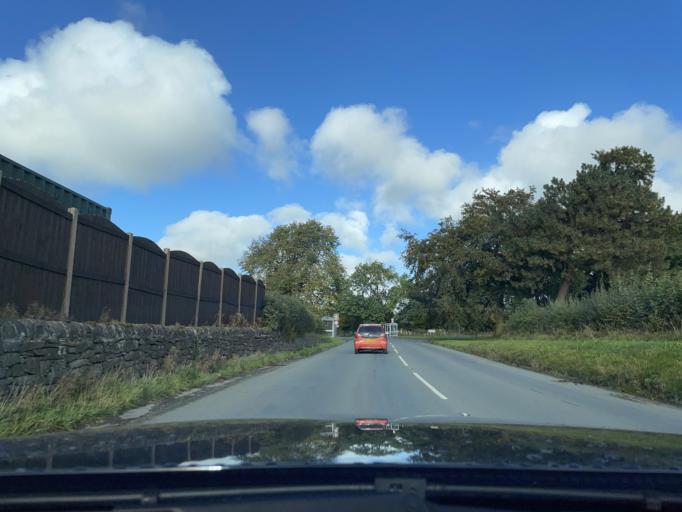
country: GB
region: England
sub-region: Derbyshire
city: Hope Valley
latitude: 53.3445
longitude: -1.7323
